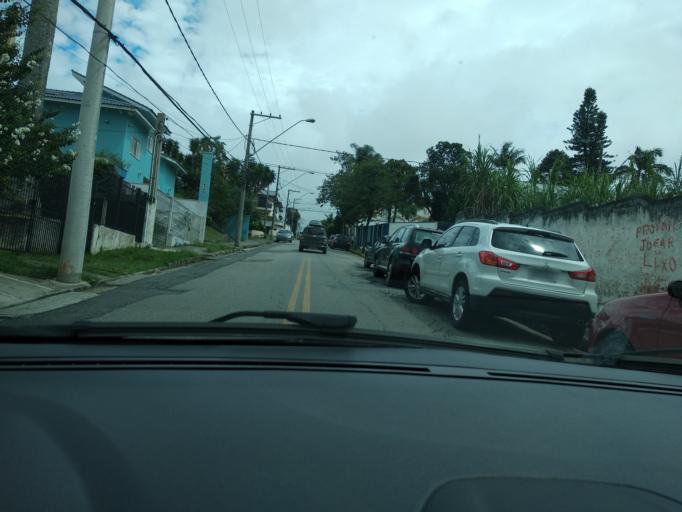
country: BR
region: Sao Paulo
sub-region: Mogi das Cruzes
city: Mogi das Cruzes
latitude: -23.5232
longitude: -46.1759
